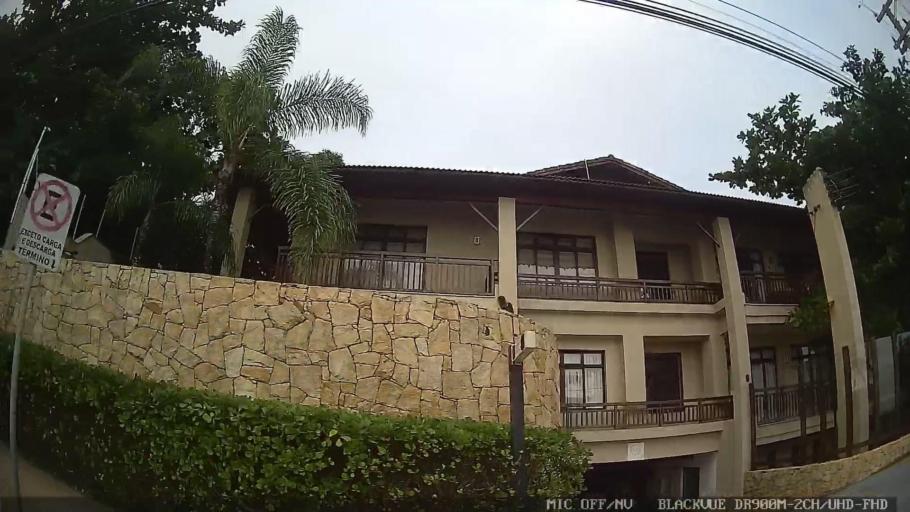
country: BR
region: Sao Paulo
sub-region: Guaruja
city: Guaruja
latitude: -23.9918
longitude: -46.2020
